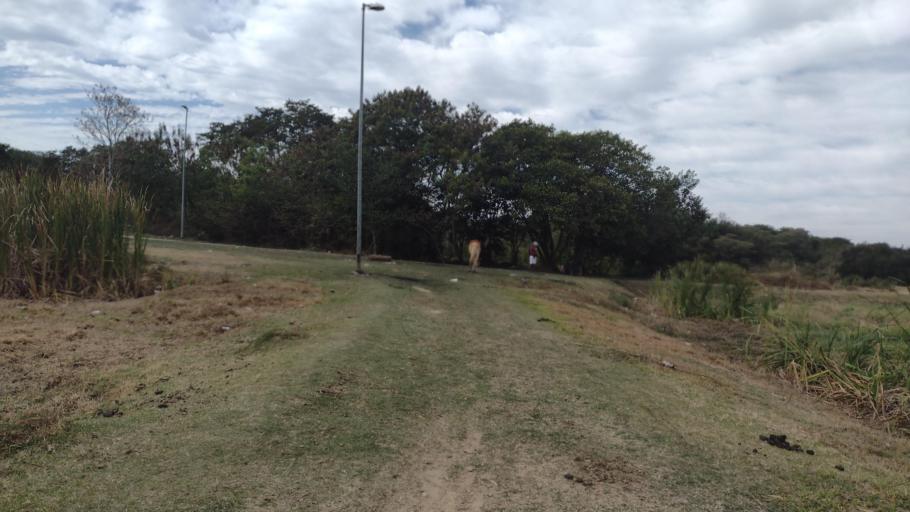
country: BR
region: Sao Paulo
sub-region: Sorocaba
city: Sorocaba
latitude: -23.4281
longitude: -47.4524
